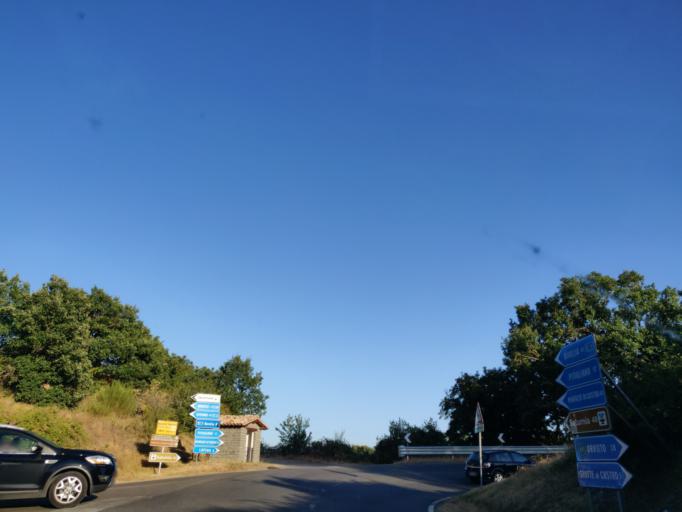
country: IT
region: Latium
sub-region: Provincia di Viterbo
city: Latera
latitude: 42.6393
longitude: 11.8389
